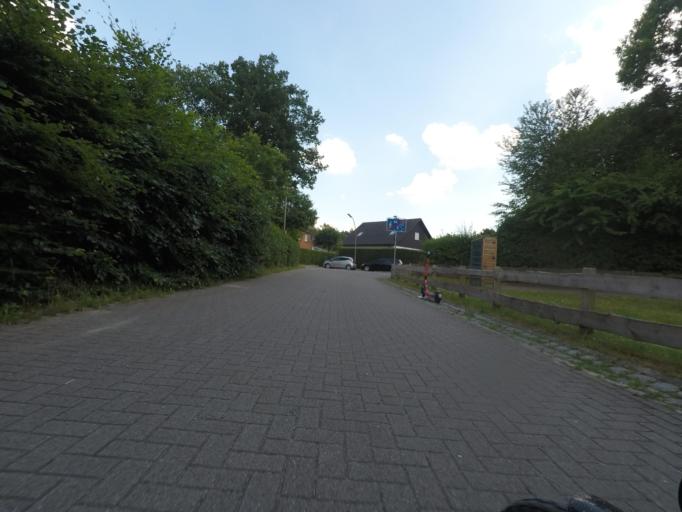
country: DE
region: Hamburg
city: Wellingsbuettel
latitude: 53.6316
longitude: 10.1021
